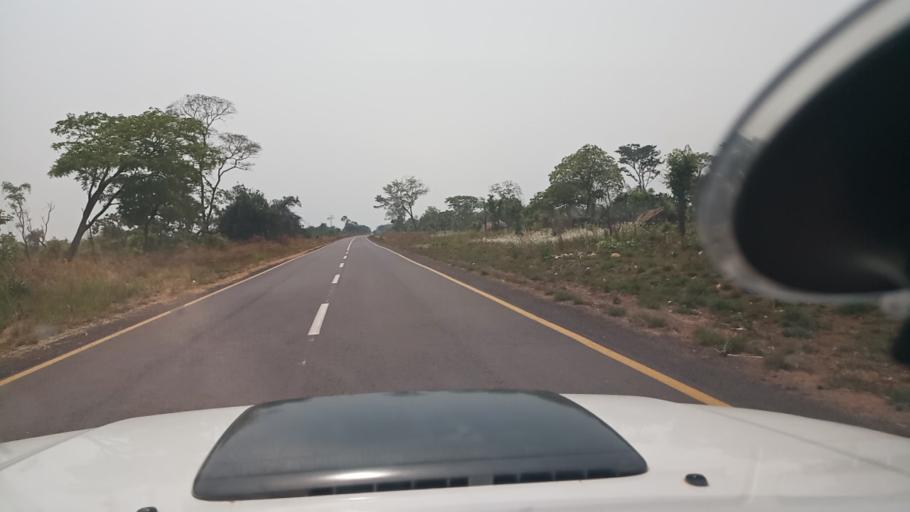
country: ZM
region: Luapula
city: Mansa
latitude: -10.9853
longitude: 28.1243
